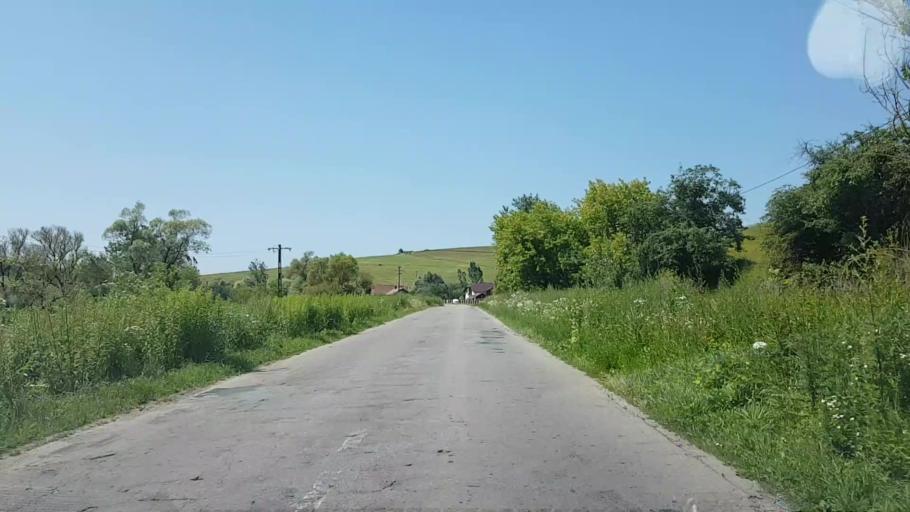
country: RO
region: Sibiu
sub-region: Oras Agnita
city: Ruja
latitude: 46.0043
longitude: 24.6755
